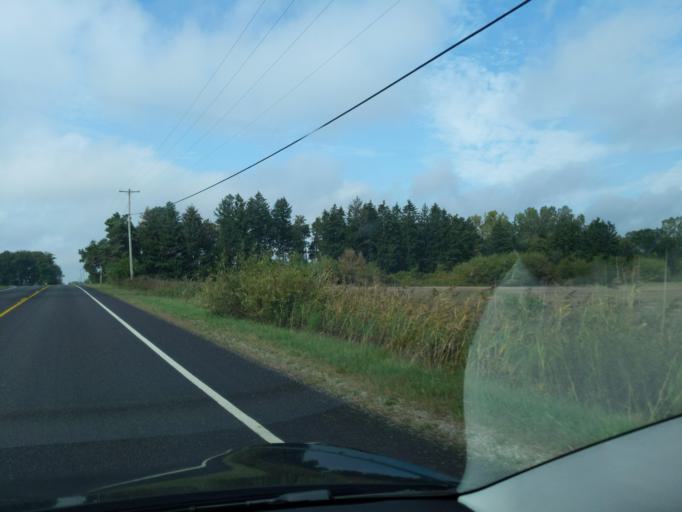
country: US
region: Michigan
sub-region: Eaton County
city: Potterville
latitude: 42.6256
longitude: -84.7180
